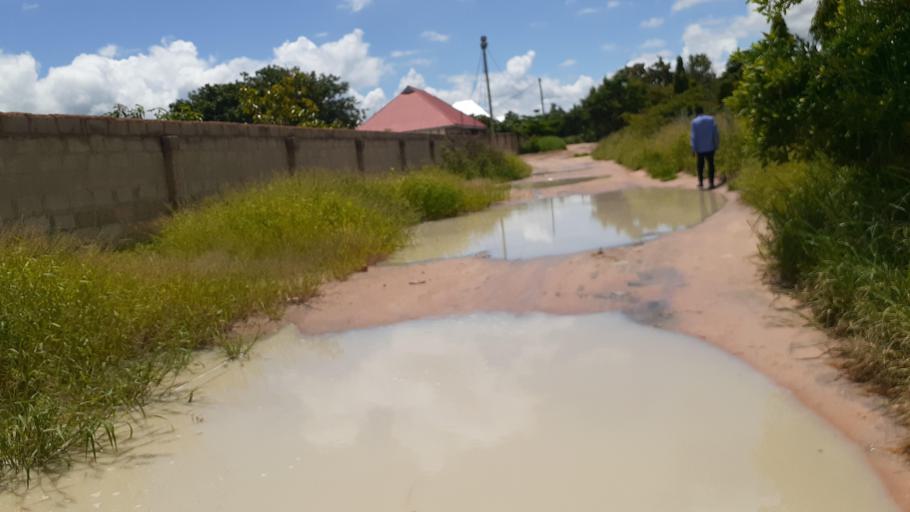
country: TZ
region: Dodoma
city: Dodoma
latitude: -6.1191
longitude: 35.7428
